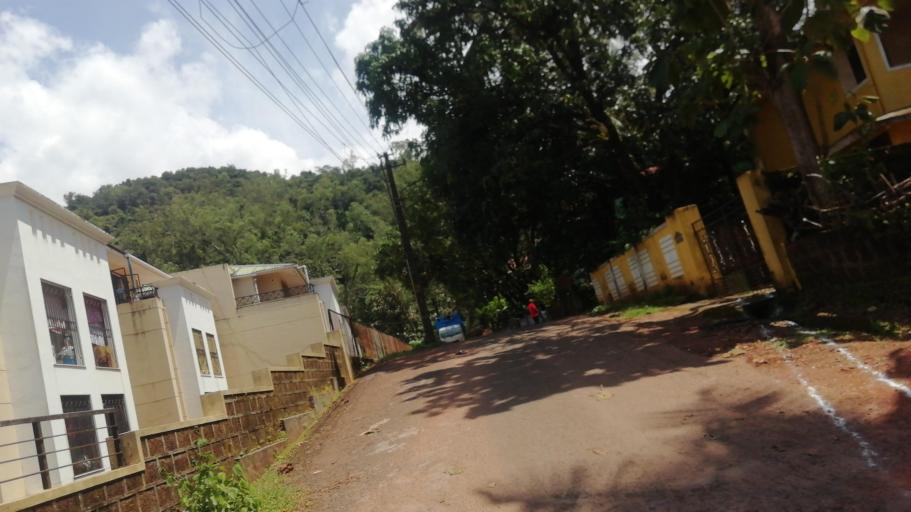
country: IN
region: Goa
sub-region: North Goa
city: Ponda
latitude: 15.3879
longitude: 74.0054
